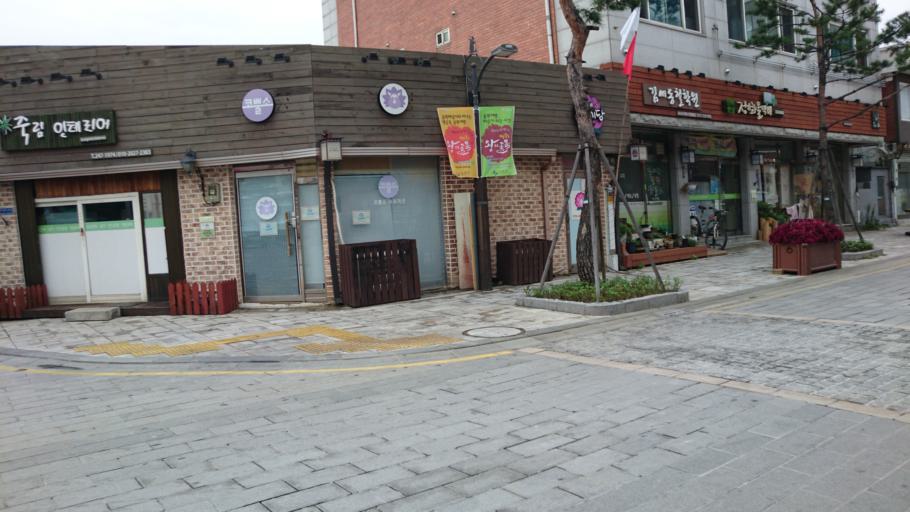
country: KR
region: Gyeonggi-do
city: Suwon-si
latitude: 37.2853
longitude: 127.0129
